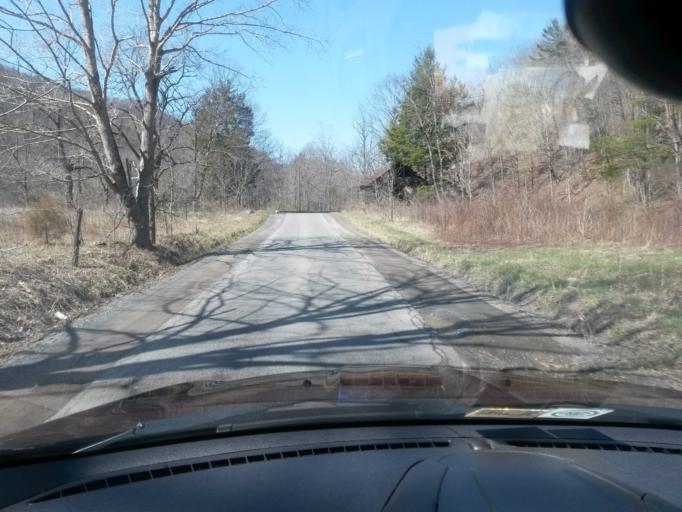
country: US
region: West Virginia
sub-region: Greenbrier County
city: White Sulphur Springs
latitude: 37.7695
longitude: -80.2796
